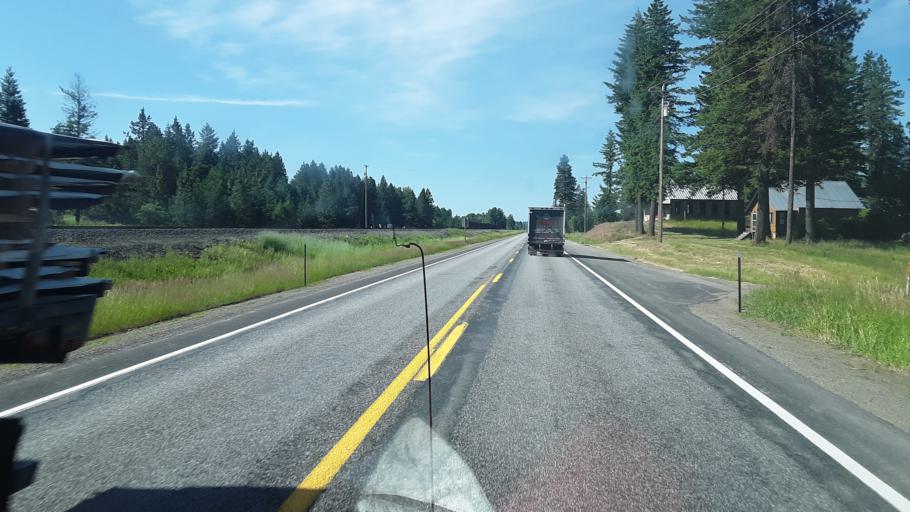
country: US
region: Idaho
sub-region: Bonner County
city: Ponderay
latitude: 48.4813
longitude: -116.4624
